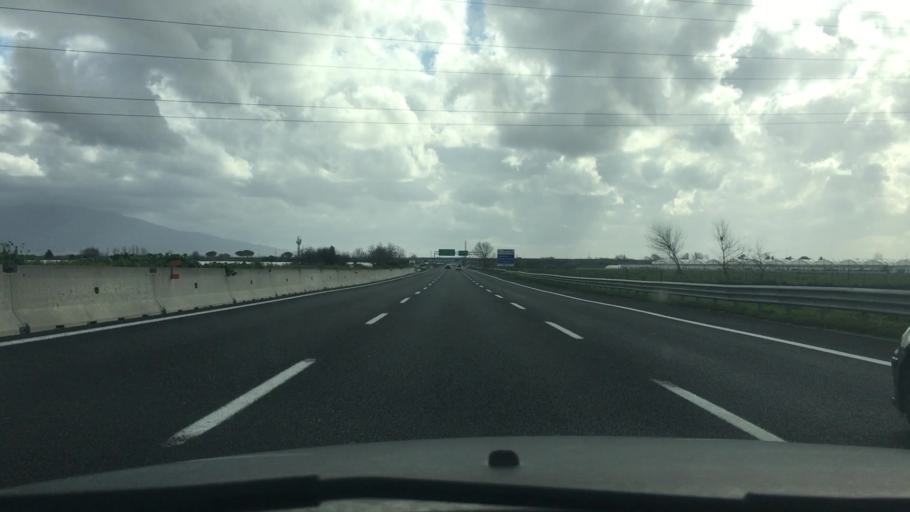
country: IT
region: Campania
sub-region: Provincia di Napoli
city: Pascarola
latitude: 40.9826
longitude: 14.3254
